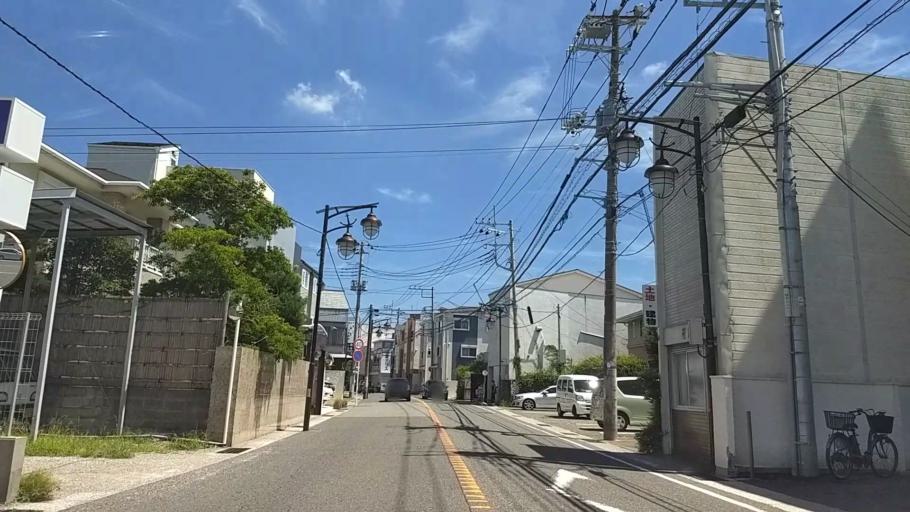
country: JP
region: Kanagawa
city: Zushi
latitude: 35.2975
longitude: 139.5735
